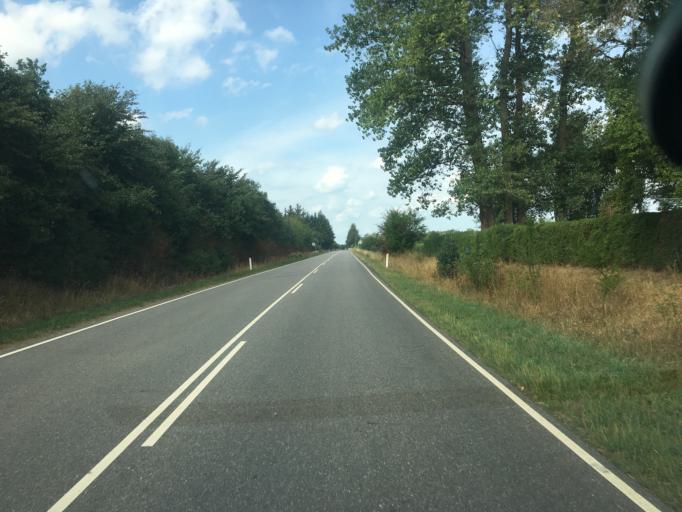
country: DK
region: South Denmark
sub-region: Aabenraa Kommune
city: Tinglev
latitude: 54.9357
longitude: 9.3215
